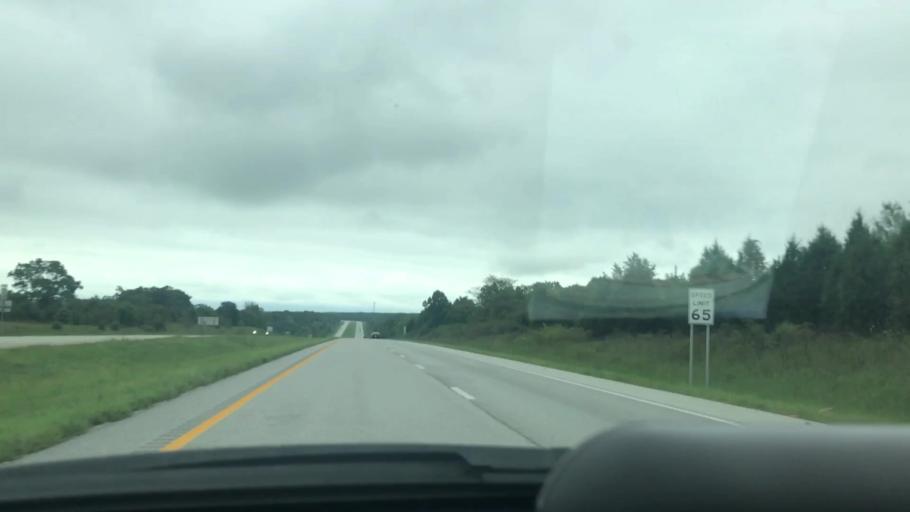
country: US
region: Missouri
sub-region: Greene County
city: Strafford
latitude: 37.3020
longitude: -93.1766
